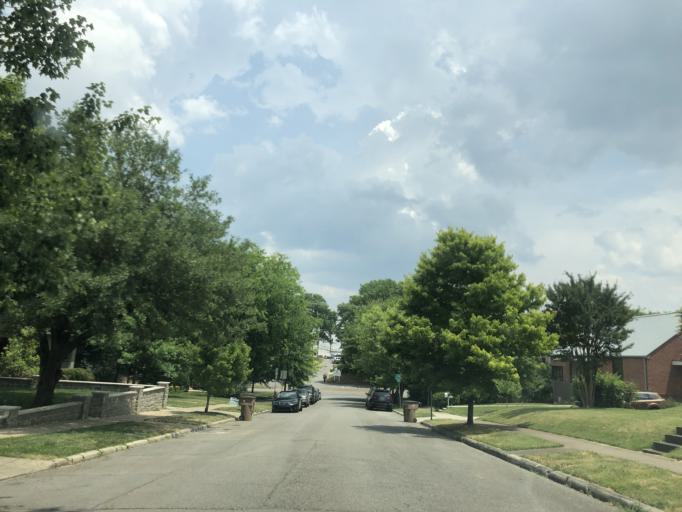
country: US
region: Tennessee
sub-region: Davidson County
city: Nashville
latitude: 36.1335
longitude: -86.8068
